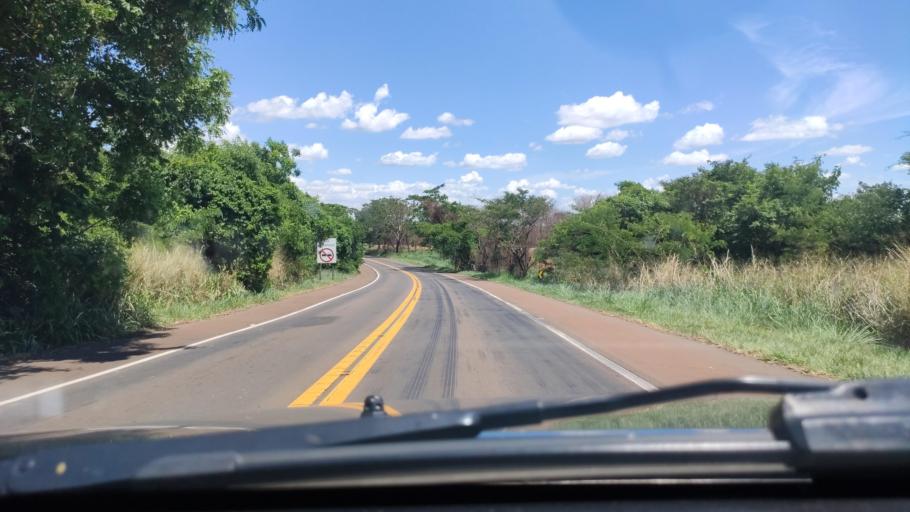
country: BR
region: Sao Paulo
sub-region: Boa Esperanca Do Sul
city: Boa Esperanca do Sul
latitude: -22.0710
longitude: -48.3655
